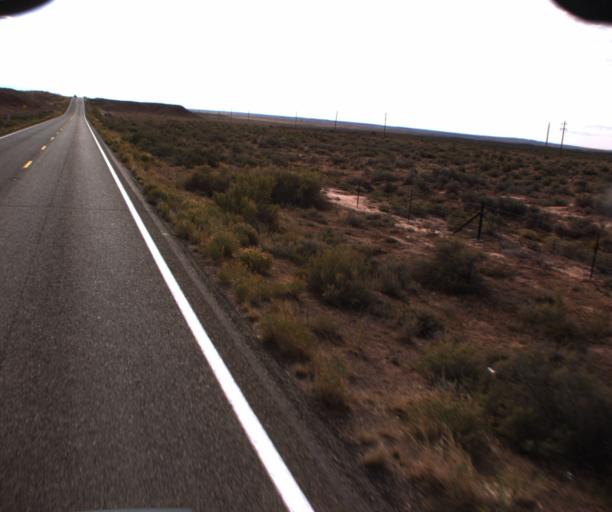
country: US
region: Arizona
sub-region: Apache County
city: Many Farms
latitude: 36.5280
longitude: -109.5028
